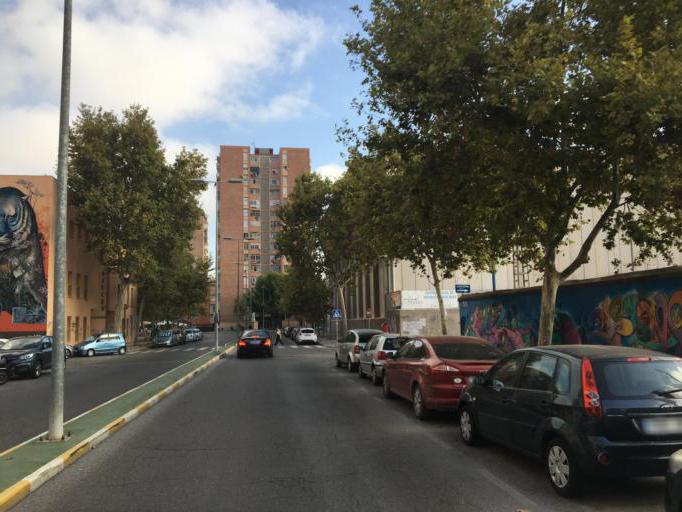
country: ES
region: Murcia
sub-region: Murcia
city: Cartagena
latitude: 37.6077
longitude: -0.9815
